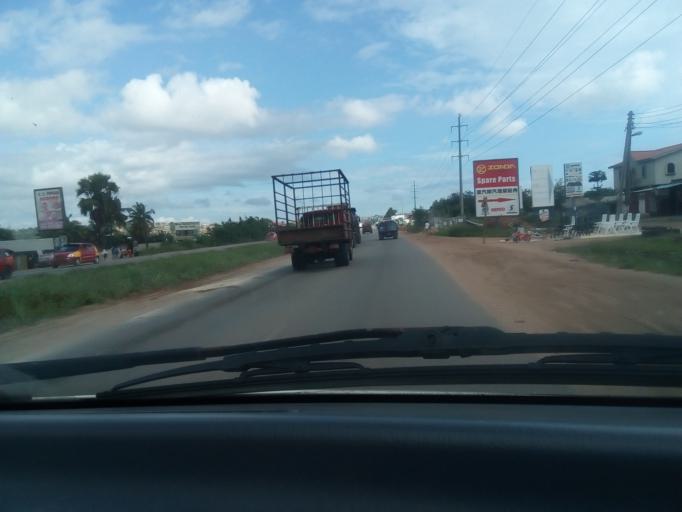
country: GH
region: Greater Accra
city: Achiaman
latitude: 5.7024
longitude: -0.2962
